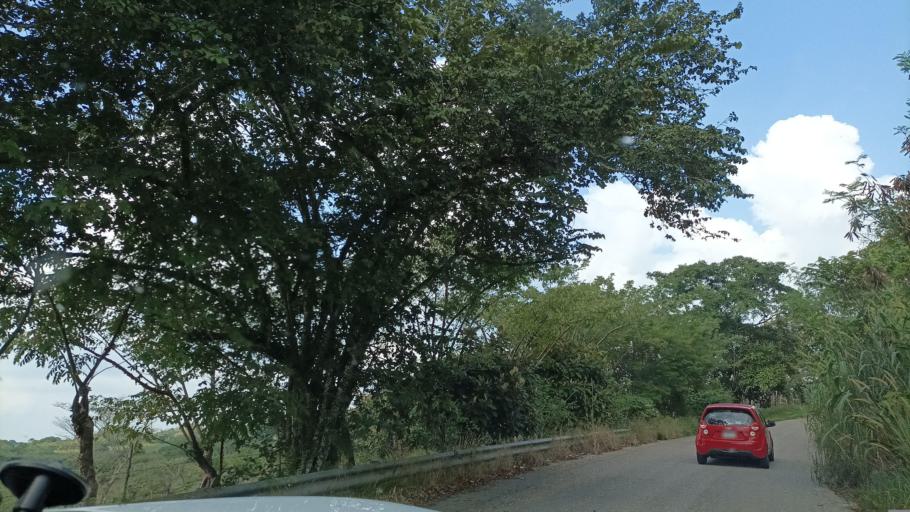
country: MX
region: Veracruz
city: Las Choapas
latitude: 17.7440
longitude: -94.1107
